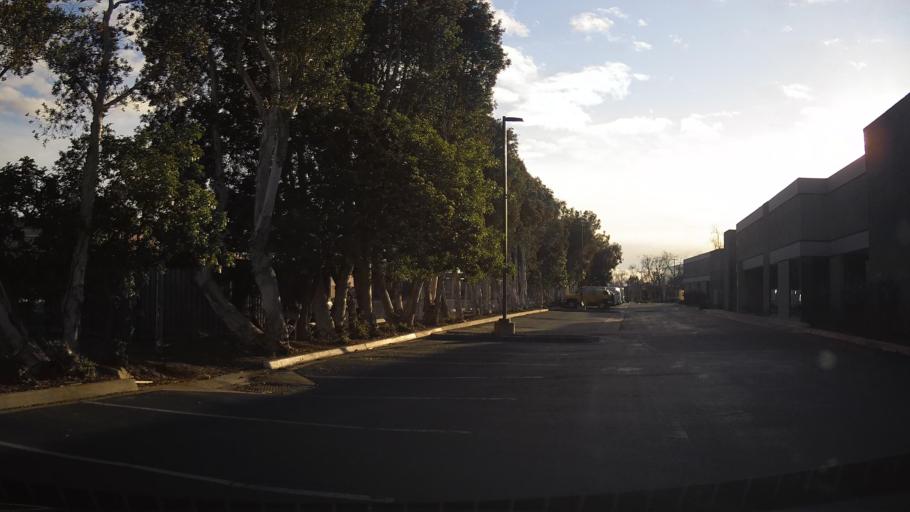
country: US
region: California
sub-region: San Diego County
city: San Diego
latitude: 32.8150
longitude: -117.1204
